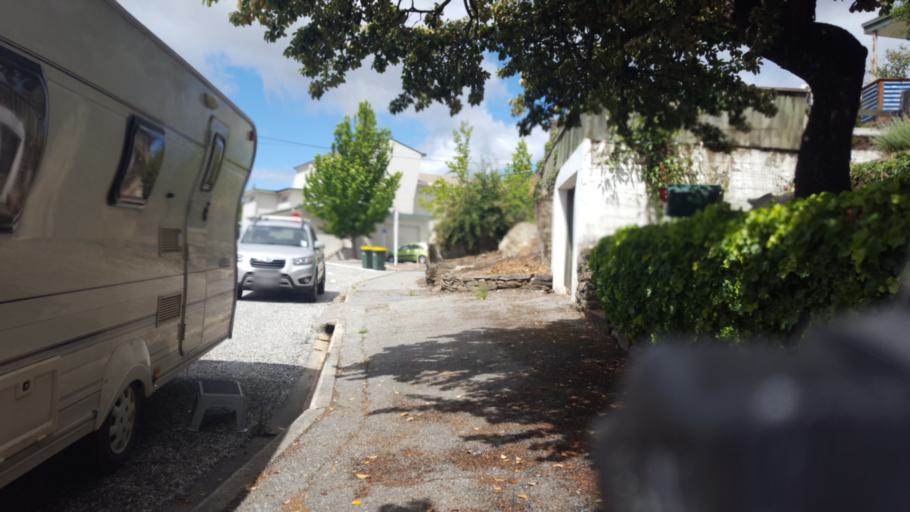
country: NZ
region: Otago
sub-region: Queenstown-Lakes District
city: Wanaka
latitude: -45.2556
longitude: 169.3945
